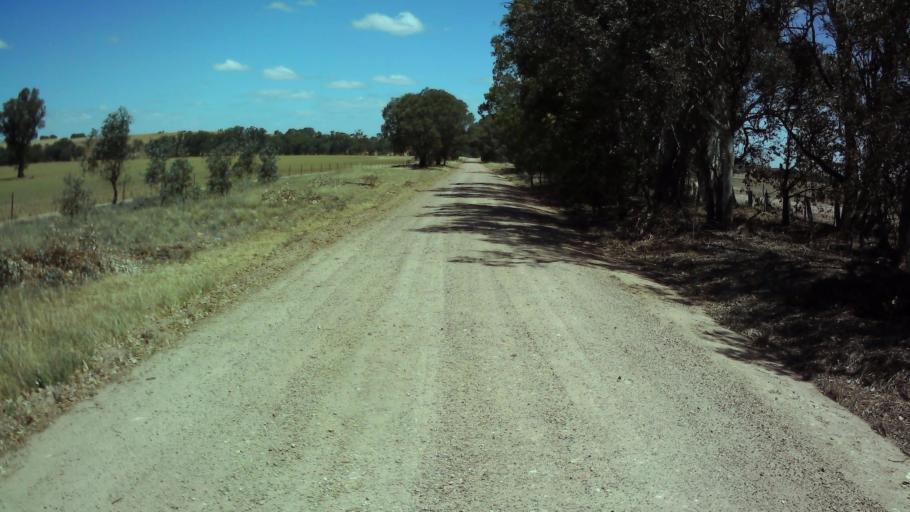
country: AU
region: New South Wales
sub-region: Weddin
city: Grenfell
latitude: -33.9271
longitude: 148.3351
